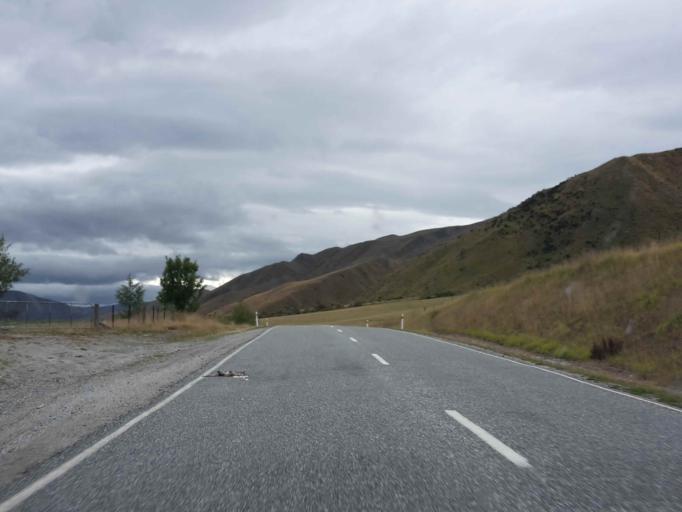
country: NZ
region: Otago
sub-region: Queenstown-Lakes District
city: Arrowtown
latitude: -44.9806
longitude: 168.8991
